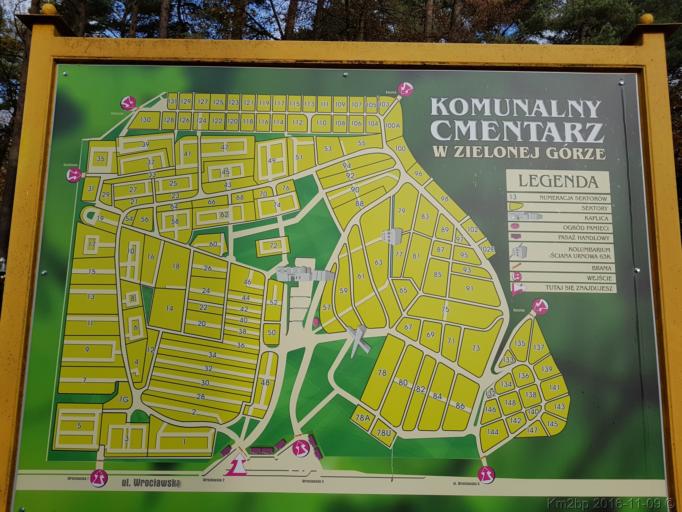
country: PL
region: Lubusz
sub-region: Zielona Gora
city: Zielona Gora
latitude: 51.9286
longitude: 15.5350
